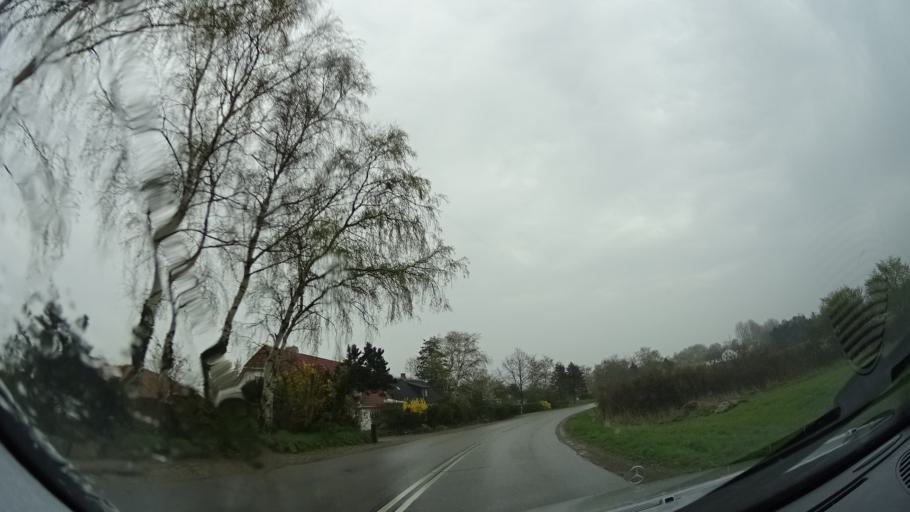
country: DK
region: Zealand
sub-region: Odsherred Kommune
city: Asnaes
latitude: 55.8545
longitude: 11.5569
